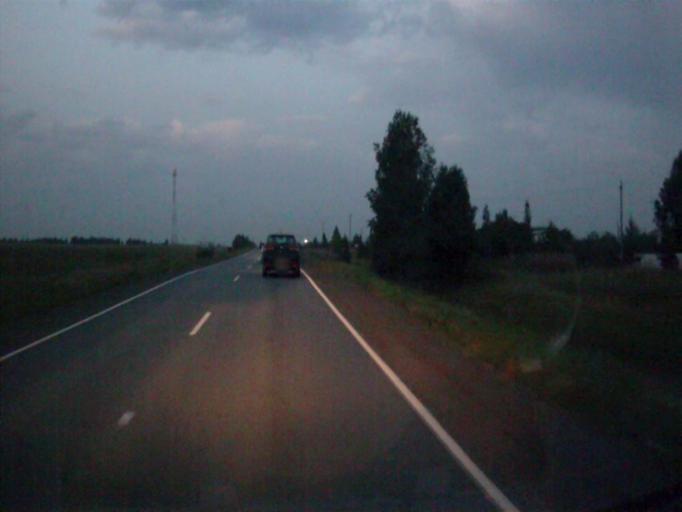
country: RU
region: Chelyabinsk
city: Poletayevo
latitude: 55.2108
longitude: 60.9107
